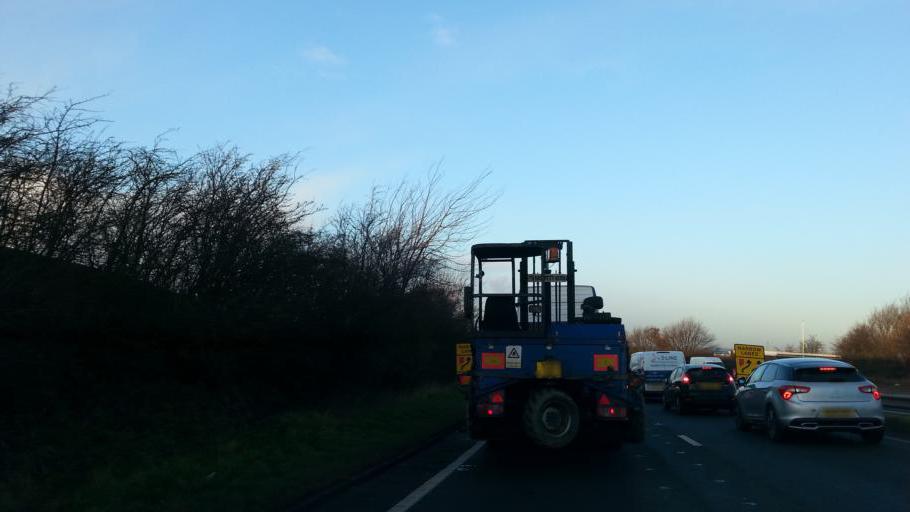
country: GB
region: England
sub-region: Leicestershire
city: Kegworth
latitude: 52.8380
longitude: -1.2972
